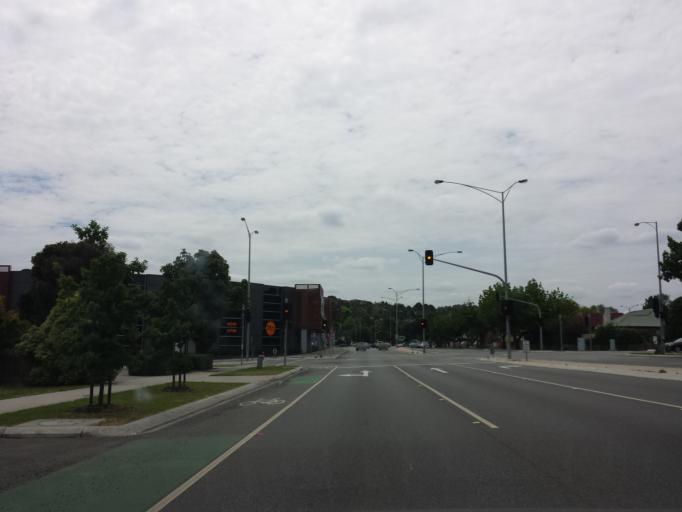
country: AU
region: Victoria
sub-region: Casey
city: Berwick
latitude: -38.0335
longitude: 145.3432
